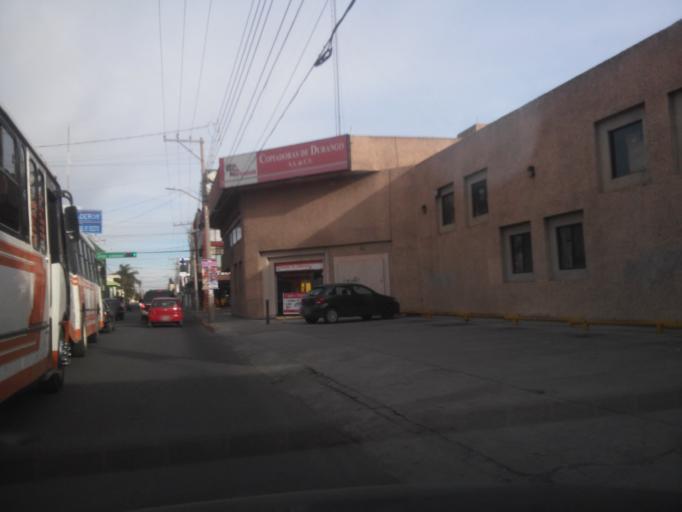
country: MX
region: Durango
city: Victoria de Durango
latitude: 24.0249
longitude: -104.6532
